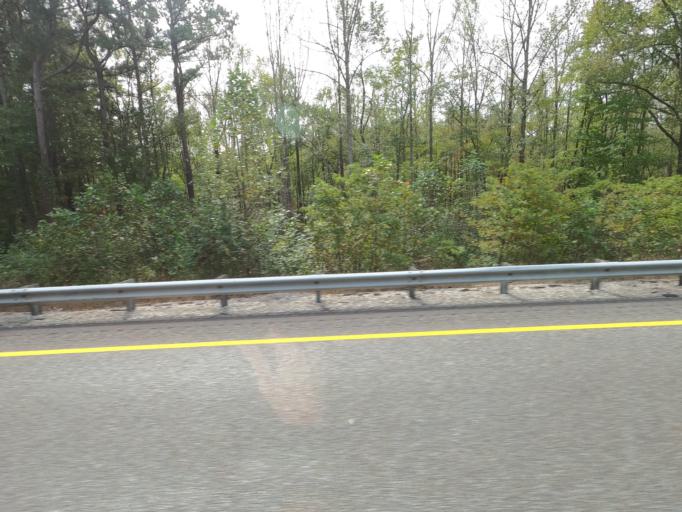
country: US
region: Tennessee
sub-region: Decatur County
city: Parsons
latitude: 35.8176
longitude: -88.2378
